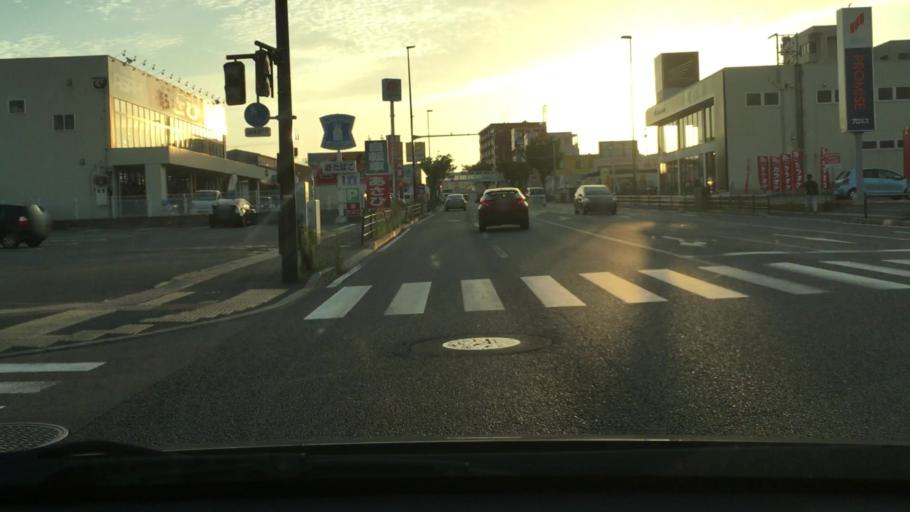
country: JP
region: Fukuoka
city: Fukuoka-shi
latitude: 33.5679
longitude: 130.3358
